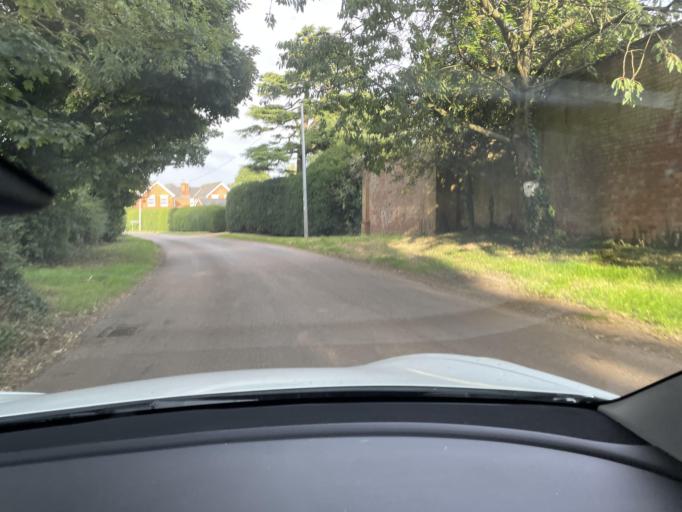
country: GB
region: England
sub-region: Northamptonshire
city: Brixworth
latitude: 52.3905
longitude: -0.9535
